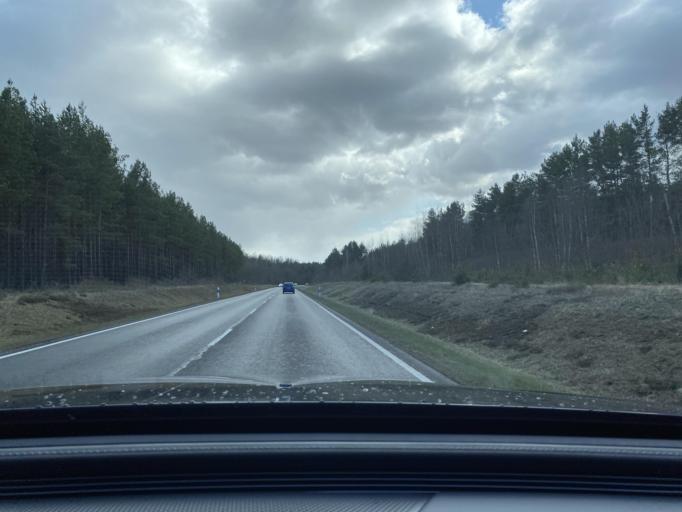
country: DE
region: Saxony
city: Weisskeissel
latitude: 51.4611
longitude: 14.6803
